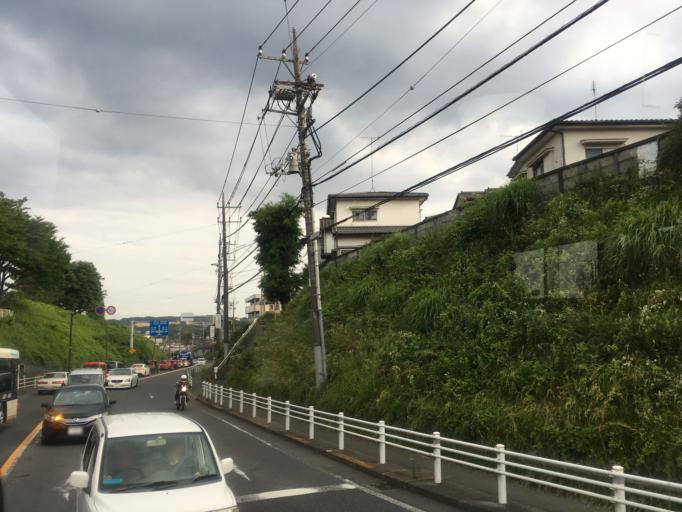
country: JP
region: Tokyo
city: Hachioji
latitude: 35.6468
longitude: 139.3368
